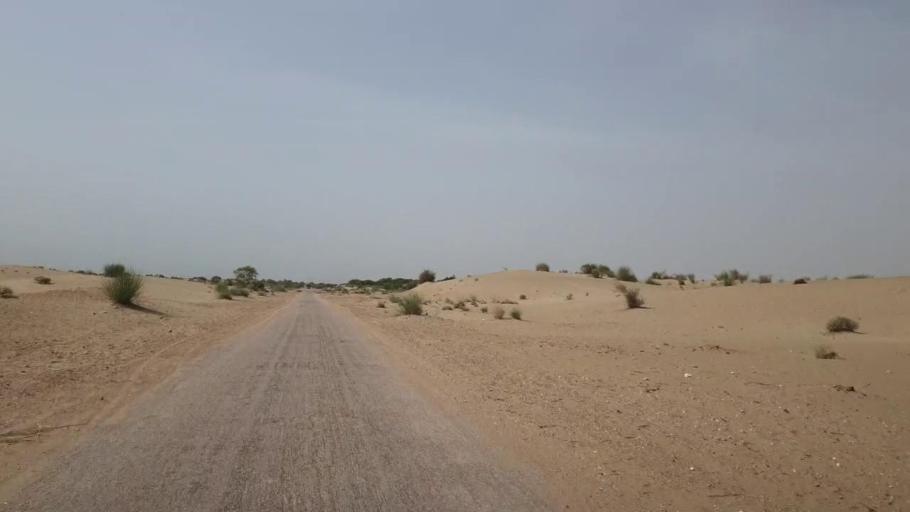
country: PK
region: Sindh
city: Bandhi
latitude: 26.5422
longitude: 68.3860
